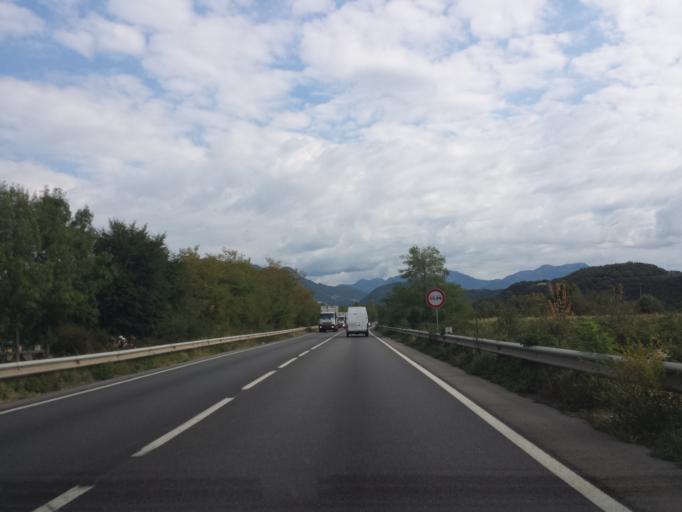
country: IT
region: Lombardy
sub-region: Provincia di Brescia
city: Prevalle
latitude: 45.5573
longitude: 10.4353
